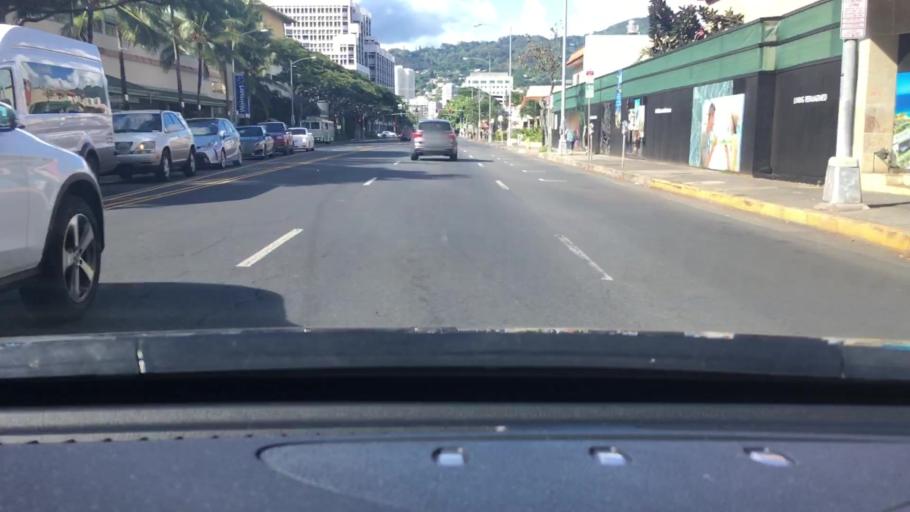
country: US
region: Hawaii
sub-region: Honolulu County
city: Honolulu
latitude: 21.2939
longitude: -157.8421
